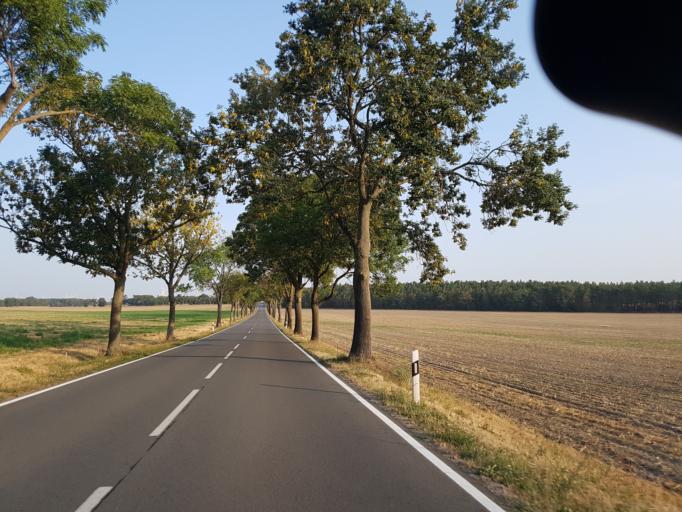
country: DE
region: Saxony-Anhalt
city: Pretzsch
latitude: 51.7380
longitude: 12.7609
